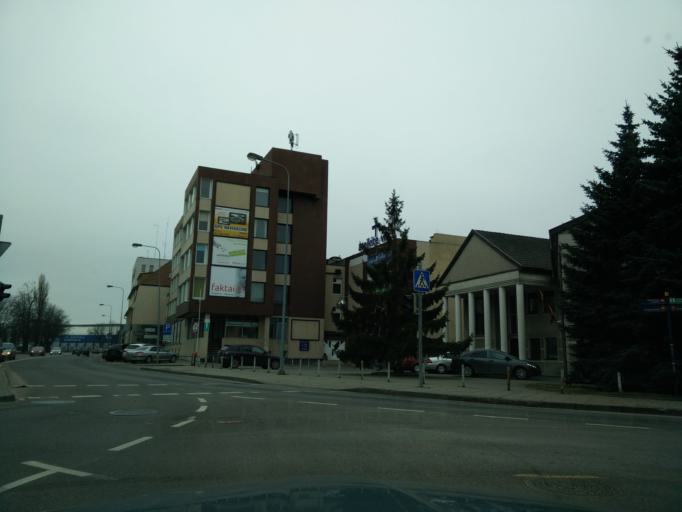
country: LT
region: Klaipedos apskritis
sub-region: Klaipeda
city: Klaipeda
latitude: 55.7024
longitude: 21.1368
